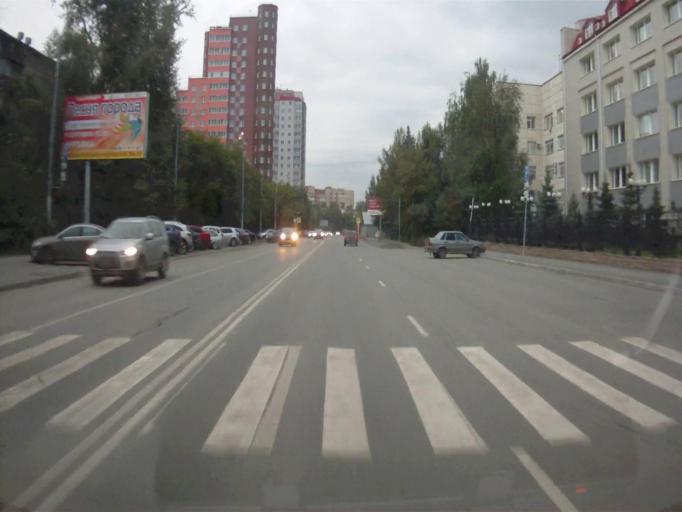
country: RU
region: Chelyabinsk
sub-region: Gorod Chelyabinsk
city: Chelyabinsk
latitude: 55.1501
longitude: 61.3986
